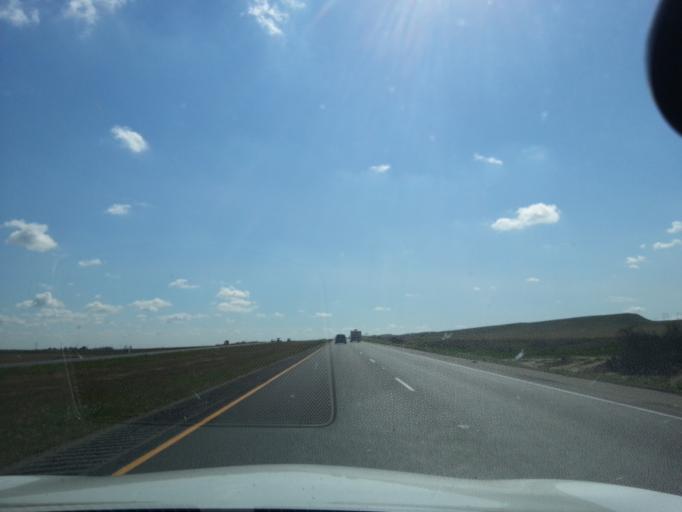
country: US
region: California
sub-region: Fresno County
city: Coalinga
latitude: 36.3498
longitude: -120.3175
